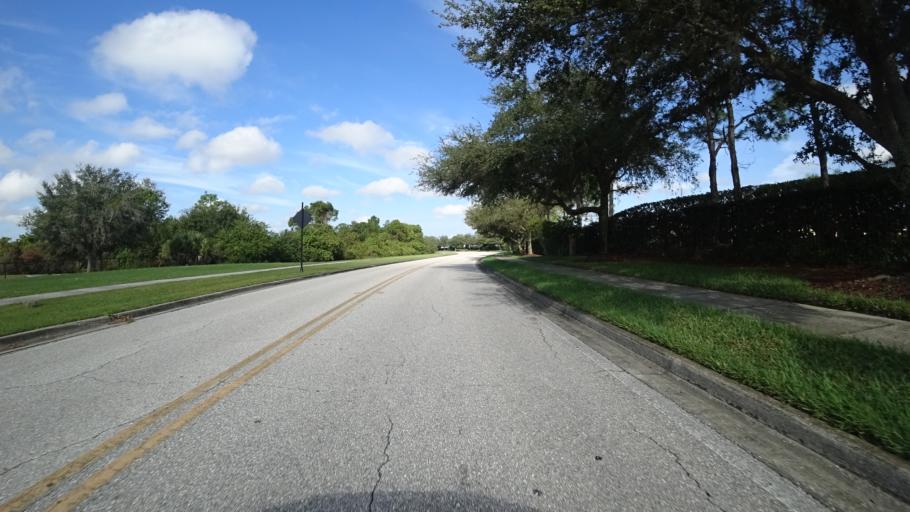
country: US
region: Florida
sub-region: Sarasota County
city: The Meadows
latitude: 27.3980
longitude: -82.4557
